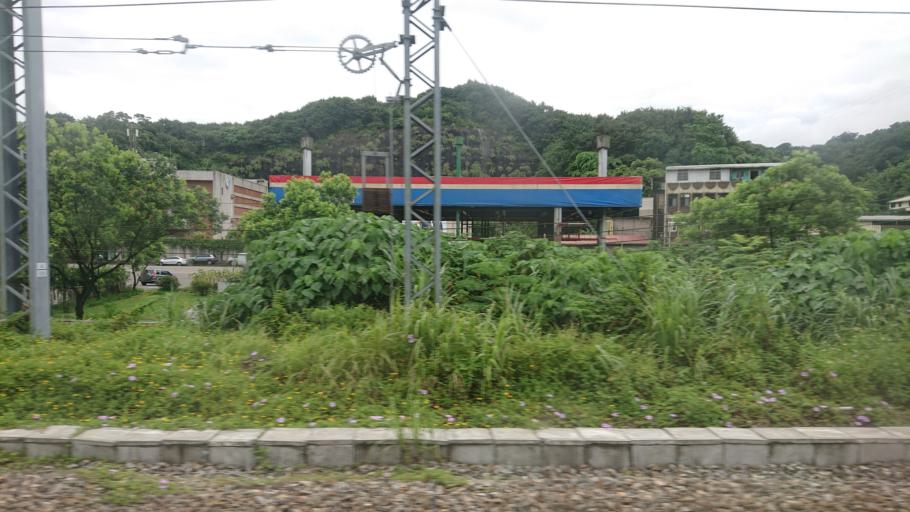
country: TW
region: Taiwan
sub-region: Keelung
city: Keelung
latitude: 25.1034
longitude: 121.7253
